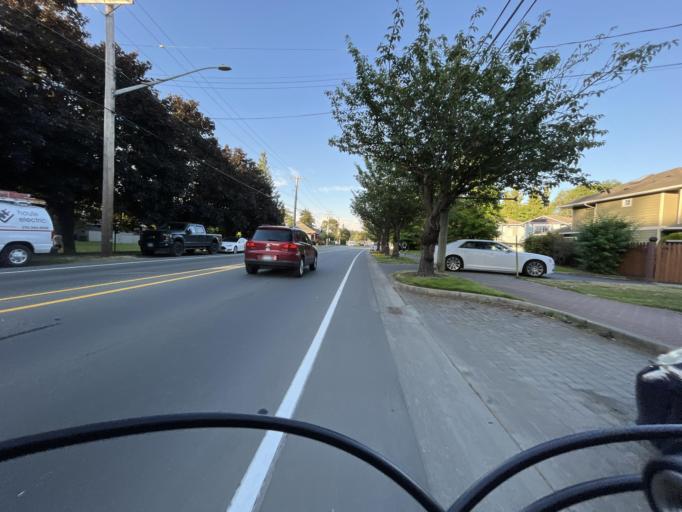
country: CA
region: British Columbia
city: Langford
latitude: 48.4506
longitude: -123.5092
